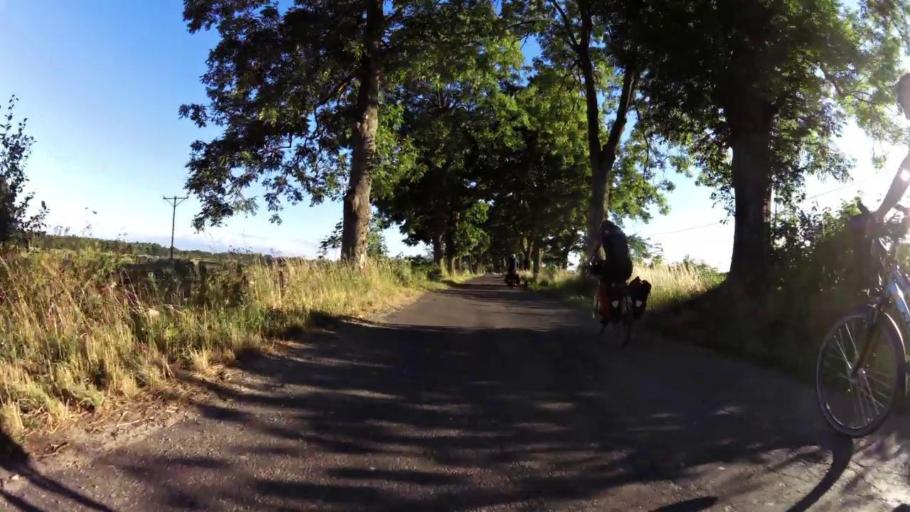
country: PL
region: West Pomeranian Voivodeship
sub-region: Powiat swidwinski
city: Swidwin
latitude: 53.7426
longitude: 15.6858
